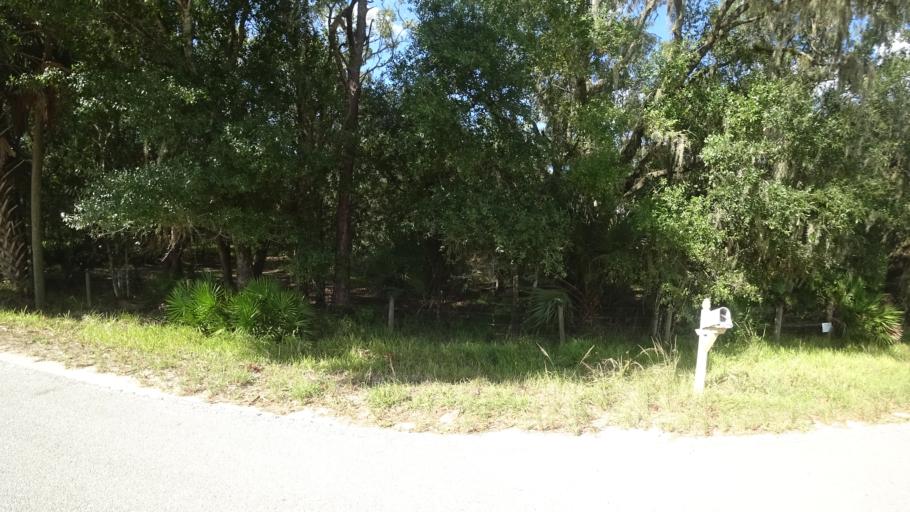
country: US
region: Florida
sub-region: DeSoto County
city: Nocatee
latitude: 27.2716
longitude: -82.0794
